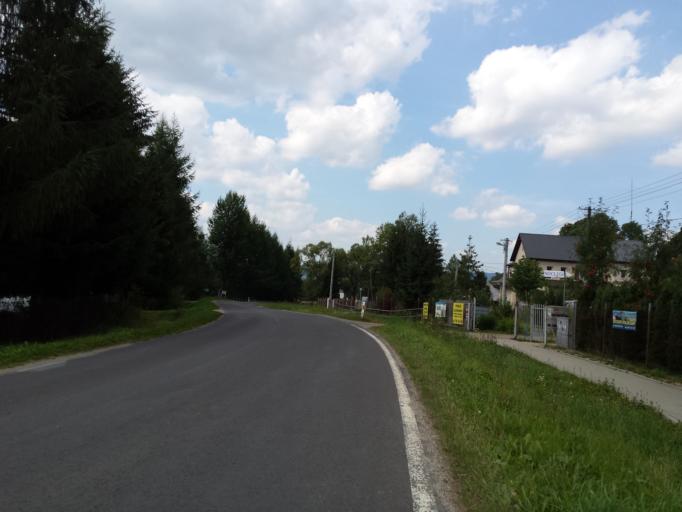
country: PL
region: Subcarpathian Voivodeship
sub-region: Powiat leski
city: Cisna
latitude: 49.1552
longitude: 22.4692
